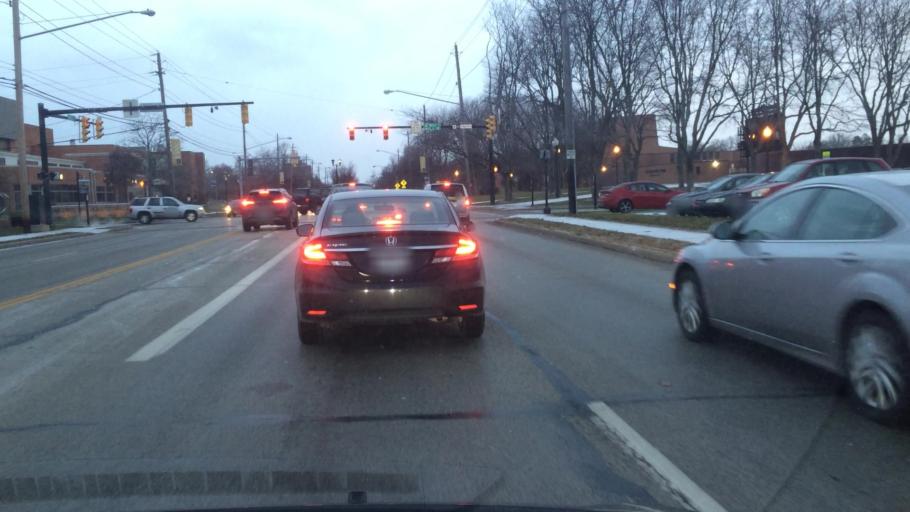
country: US
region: Ohio
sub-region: Cuyahoga County
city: Berea
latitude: 41.3725
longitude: -81.8462
